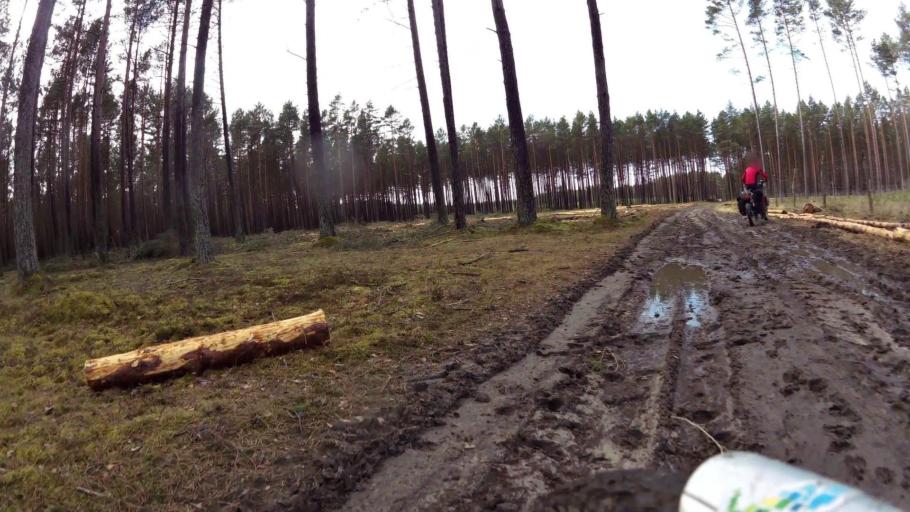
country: PL
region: Pomeranian Voivodeship
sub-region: Powiat bytowski
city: Kolczyglowy
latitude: 54.2005
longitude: 17.2308
